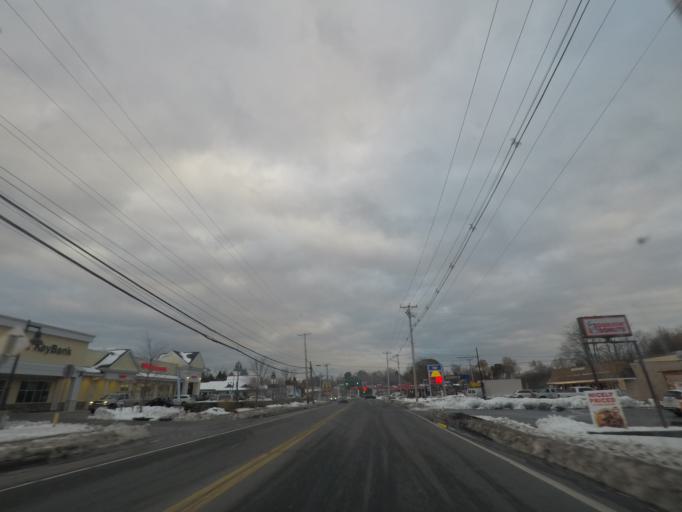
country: US
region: New York
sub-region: Orange County
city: Balmville
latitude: 41.5269
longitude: -74.0339
